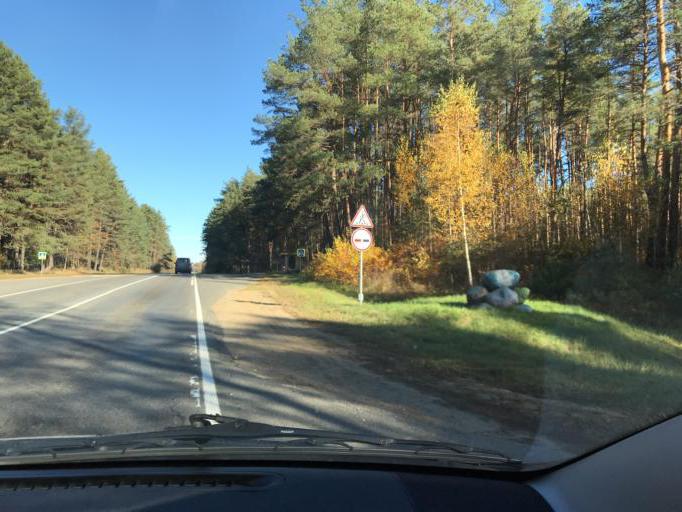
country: BY
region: Vitebsk
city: Polatsk
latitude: 55.3188
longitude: 28.7787
